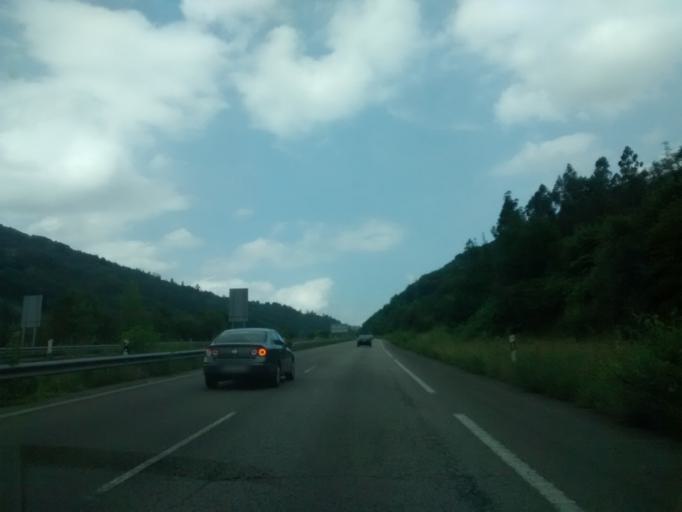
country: ES
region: Asturias
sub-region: Province of Asturias
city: Mieres
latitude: 43.2669
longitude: -5.7765
